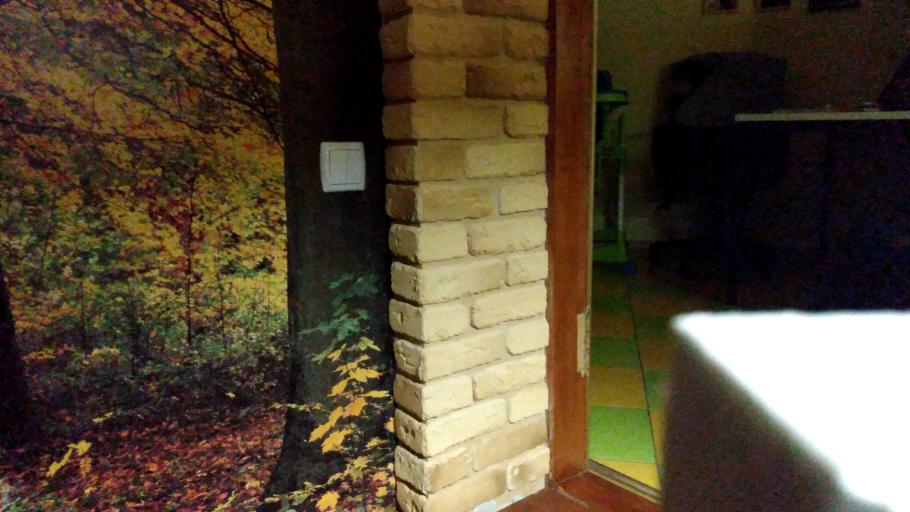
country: RU
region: Vologda
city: Lipin Bor
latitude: 60.7633
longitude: 38.0464
